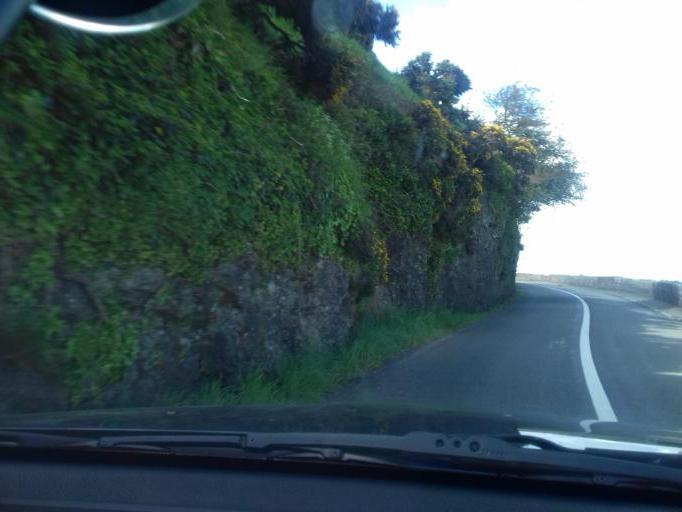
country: IE
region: Munster
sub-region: Waterford
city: Dunmore East
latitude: 52.2403
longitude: -6.9750
